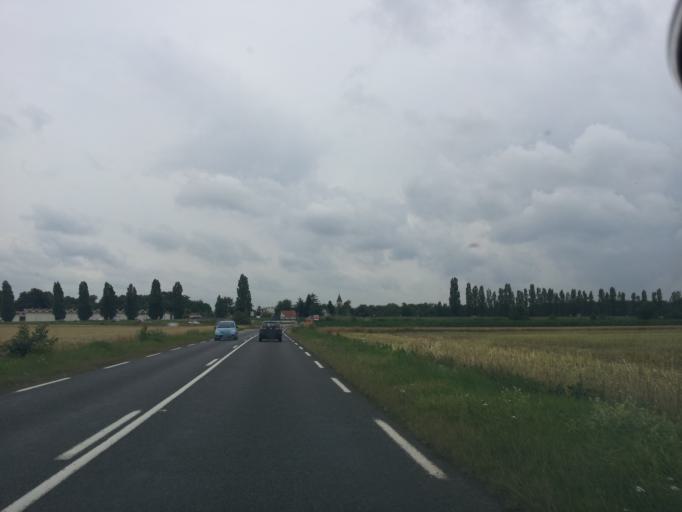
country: FR
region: Ile-de-France
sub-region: Departement de l'Essonne
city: Vert-le-Grand
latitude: 48.5710
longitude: 2.3681
